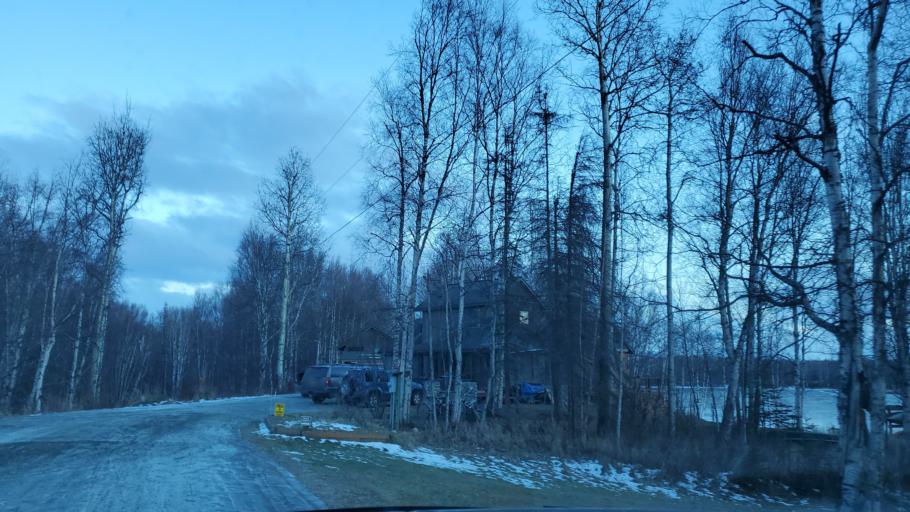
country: US
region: Alaska
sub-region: Matanuska-Susitna Borough
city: Lakes
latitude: 61.6641
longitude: -149.3231
